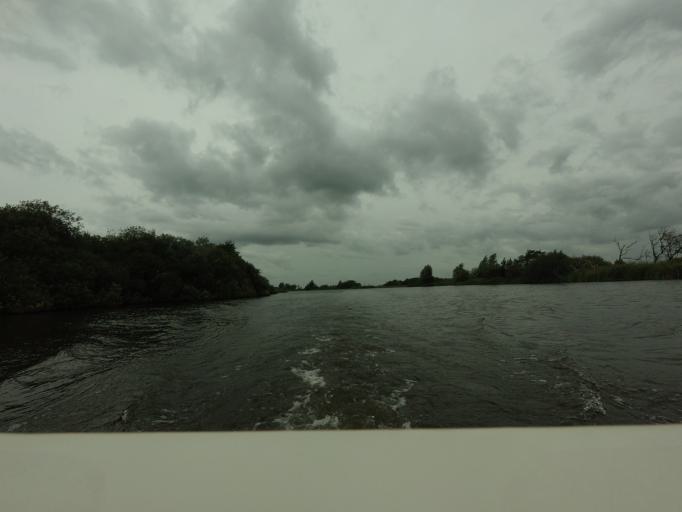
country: NL
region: Friesland
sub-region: Gemeente Boarnsterhim
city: Warten
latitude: 53.1008
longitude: 5.9128
